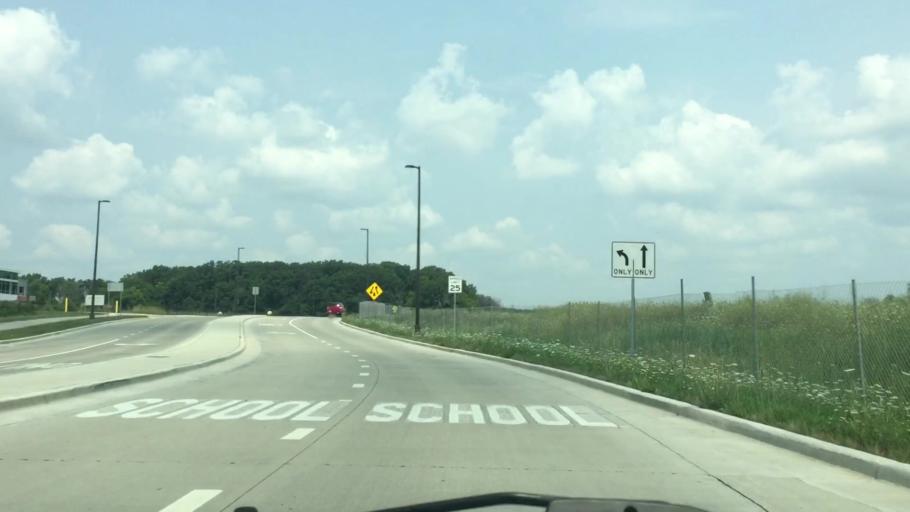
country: US
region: Wisconsin
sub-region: Milwaukee County
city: Greendale
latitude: 42.9019
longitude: -87.9411
